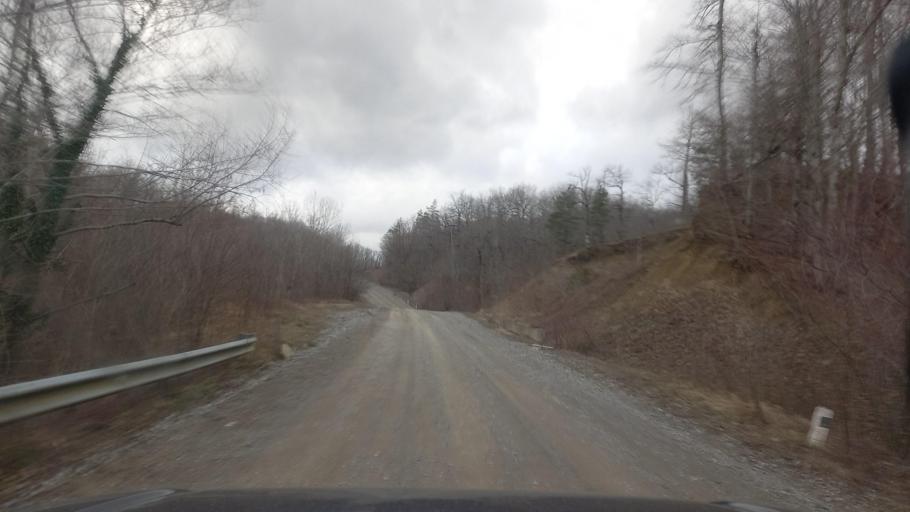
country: RU
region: Krasnodarskiy
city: Dzhubga
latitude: 44.5391
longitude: 38.7848
